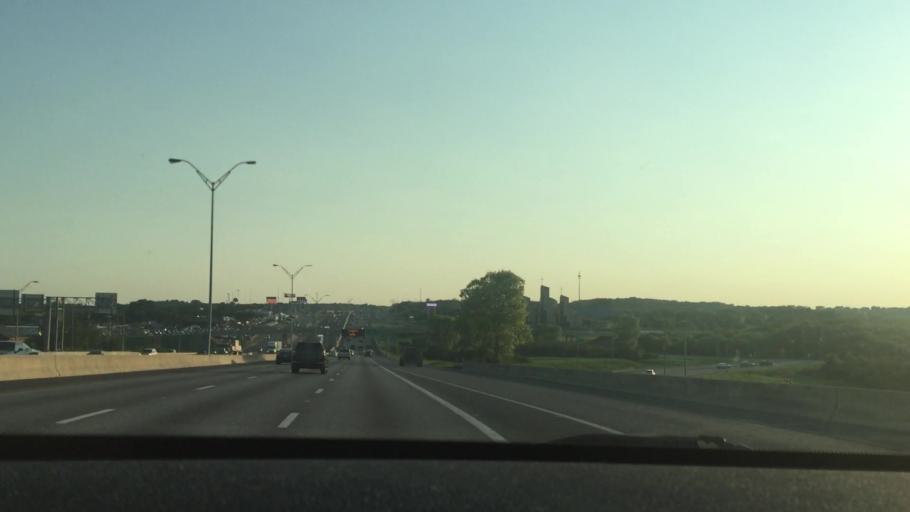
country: US
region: Texas
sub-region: Bexar County
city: Live Oak
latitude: 29.5637
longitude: -98.3383
